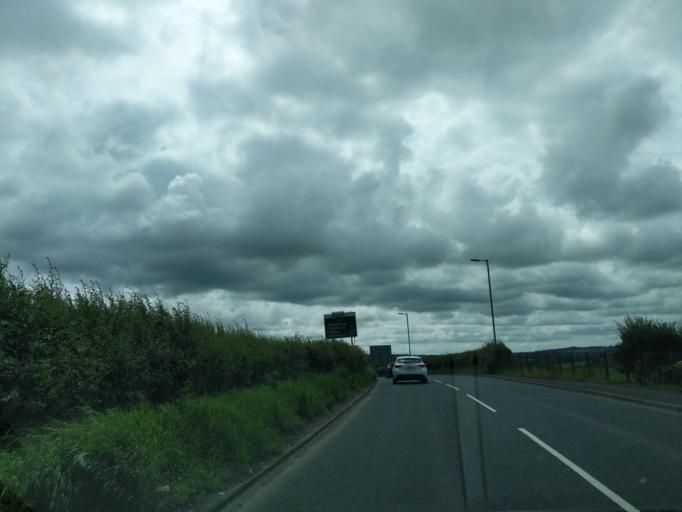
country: GB
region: Scotland
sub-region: South Lanarkshire
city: Larkhall
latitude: 55.7123
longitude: -3.9607
